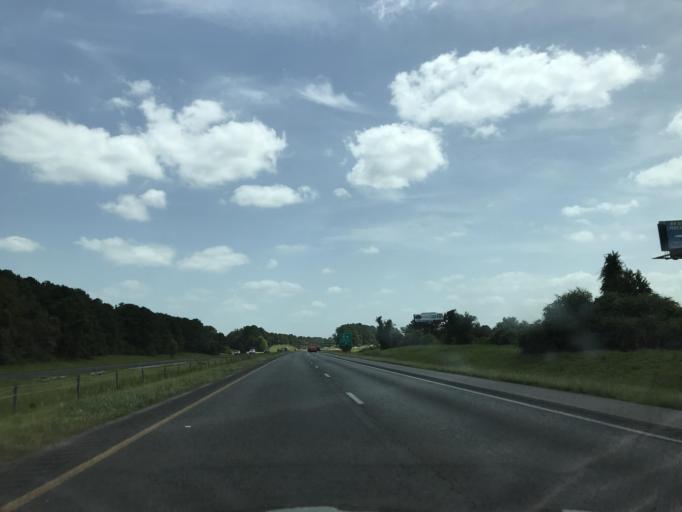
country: US
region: North Carolina
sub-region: Duplin County
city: Kenansville
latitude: 34.9227
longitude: -78.0298
